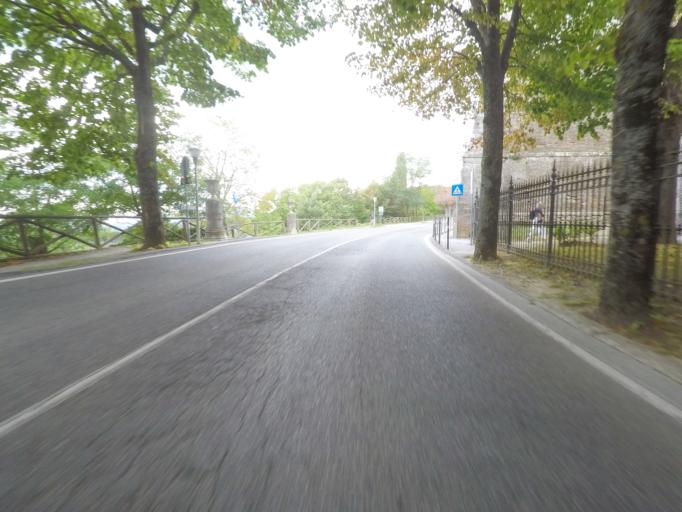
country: IT
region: Tuscany
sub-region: Provincia di Siena
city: Montepulciano
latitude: 43.0972
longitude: 11.7866
